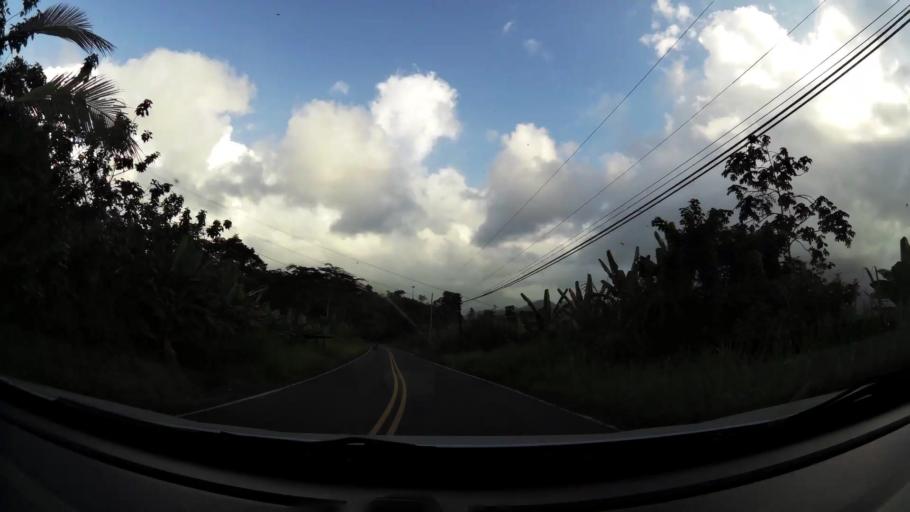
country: CR
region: Limon
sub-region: Canton de Siquirres
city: Siquirres
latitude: 10.0019
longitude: -83.5760
